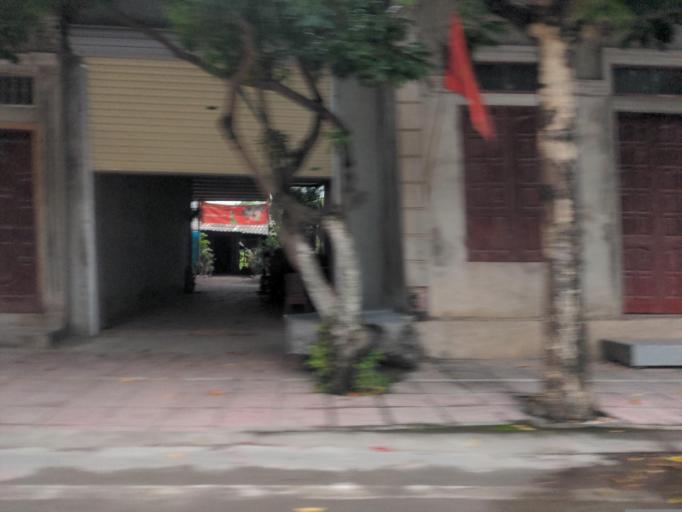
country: VN
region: Ninh Binh
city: Thi Tran Tam Diep
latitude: 20.2142
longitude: 105.9337
